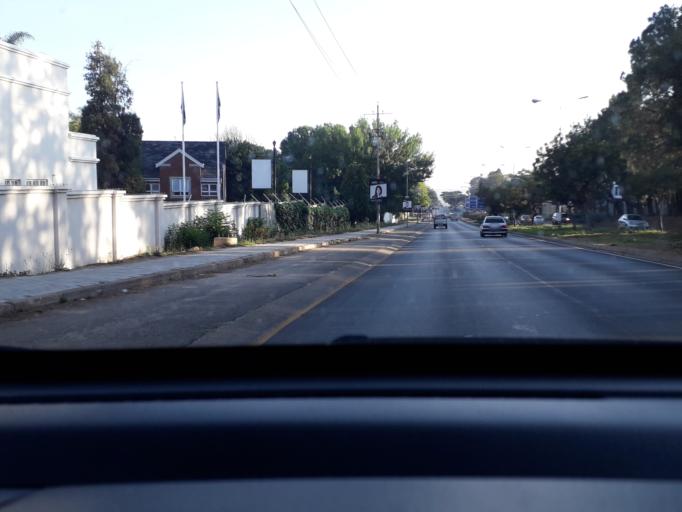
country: ZA
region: Gauteng
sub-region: City of Johannesburg Metropolitan Municipality
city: Modderfontein
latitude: -26.0863
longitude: 28.0591
